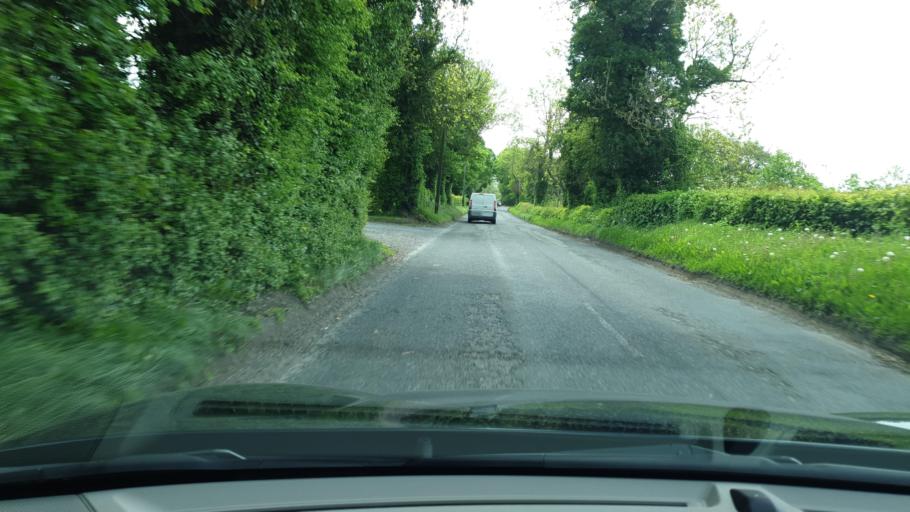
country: IE
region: Ulster
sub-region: An Cabhan
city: Kingscourt
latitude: 53.8392
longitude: -6.7687
